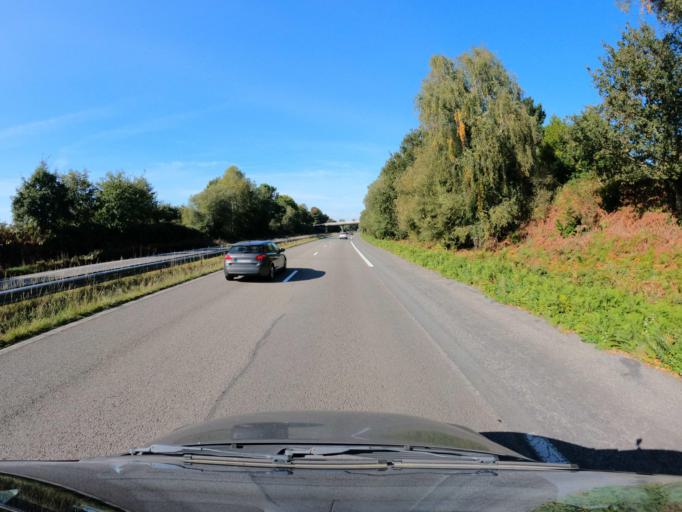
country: FR
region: Pays de la Loire
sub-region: Departement de la Loire-Atlantique
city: Missillac
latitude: 47.4714
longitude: -2.1696
